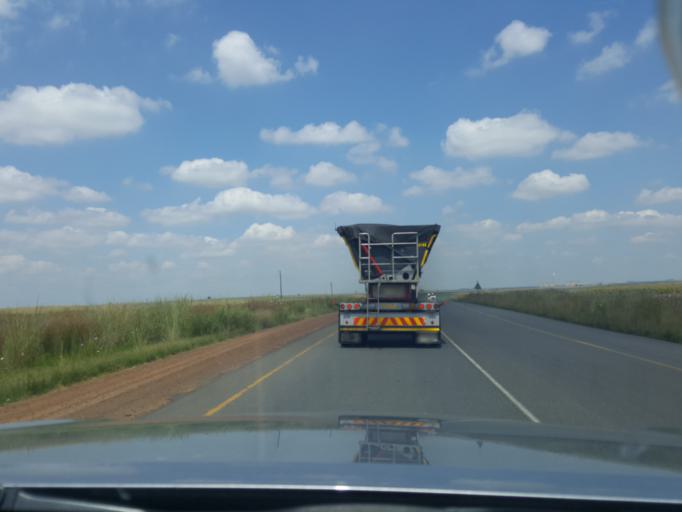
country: ZA
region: Mpumalanga
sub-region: Nkangala District Municipality
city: Witbank
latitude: -26.0171
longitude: 29.4219
